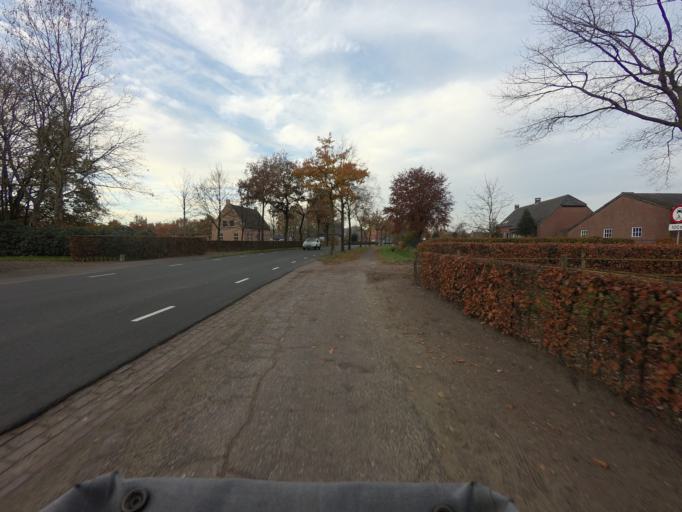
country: NL
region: North Brabant
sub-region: Gemeente Breda
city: Breda
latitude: 51.5044
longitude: 4.7934
